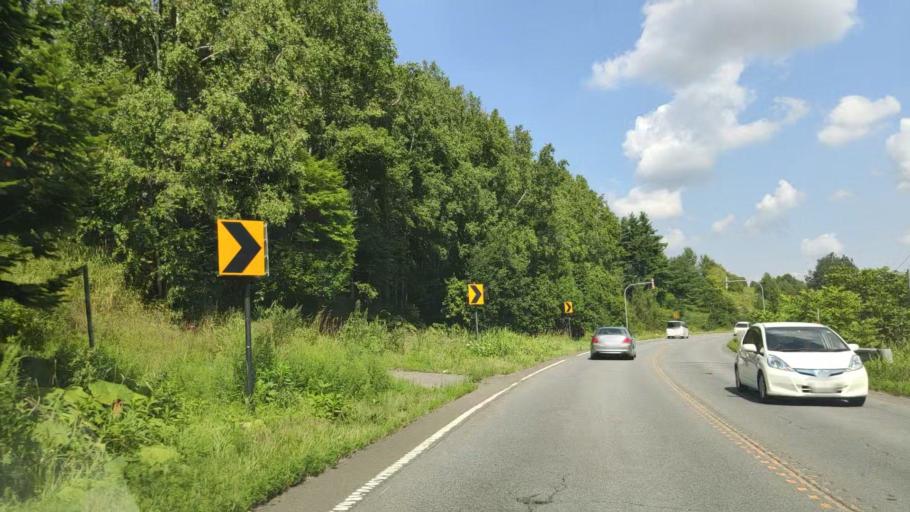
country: JP
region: Hokkaido
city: Shimo-furano
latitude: 43.5565
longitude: 142.4349
